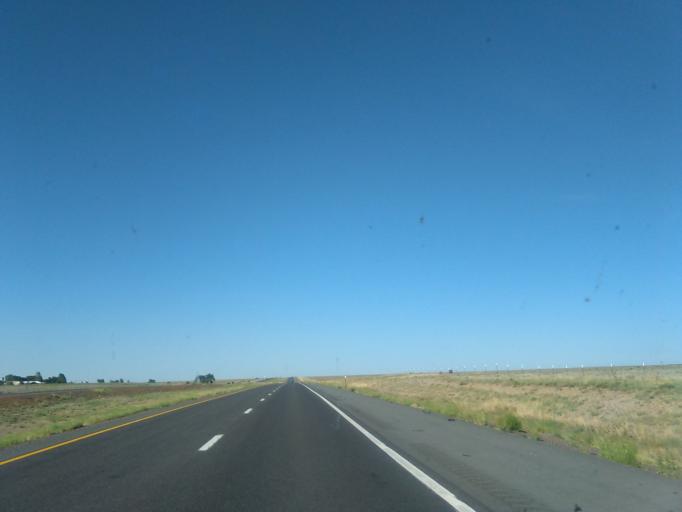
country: US
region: New Mexico
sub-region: San Miguel County
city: Las Vegas
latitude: 35.6813
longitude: -105.1609
